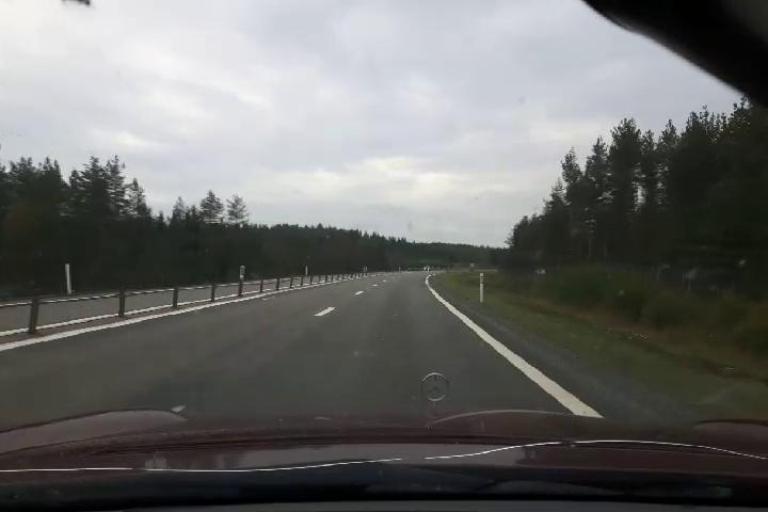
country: SE
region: Vaesternorrland
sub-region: Haernoesands Kommun
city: Haernoesand
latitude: 62.7219
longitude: 17.9200
